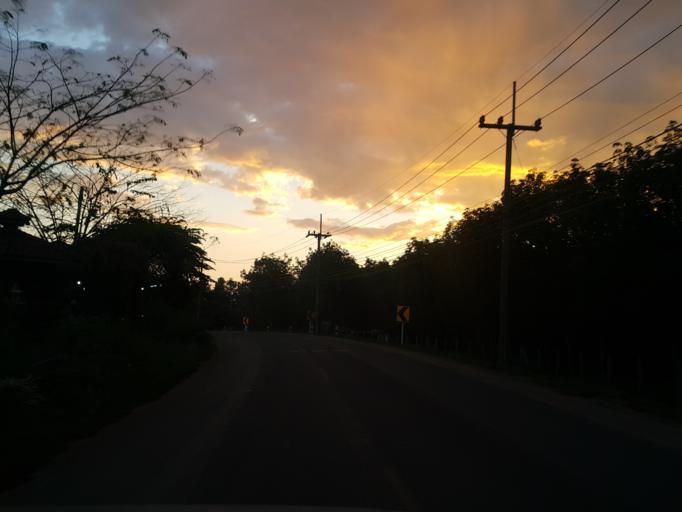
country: TH
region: Mae Hong Son
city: Khun Yuam
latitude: 18.8453
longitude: 97.9579
